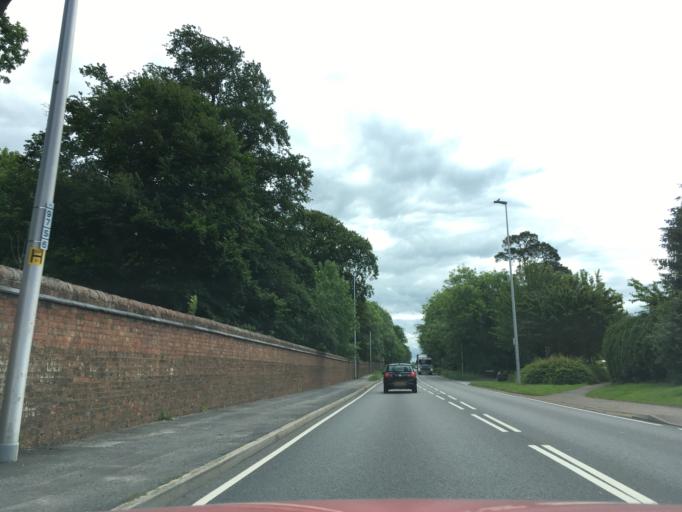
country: GB
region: England
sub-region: Northamptonshire
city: Towcester
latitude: 52.1273
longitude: -0.9818
